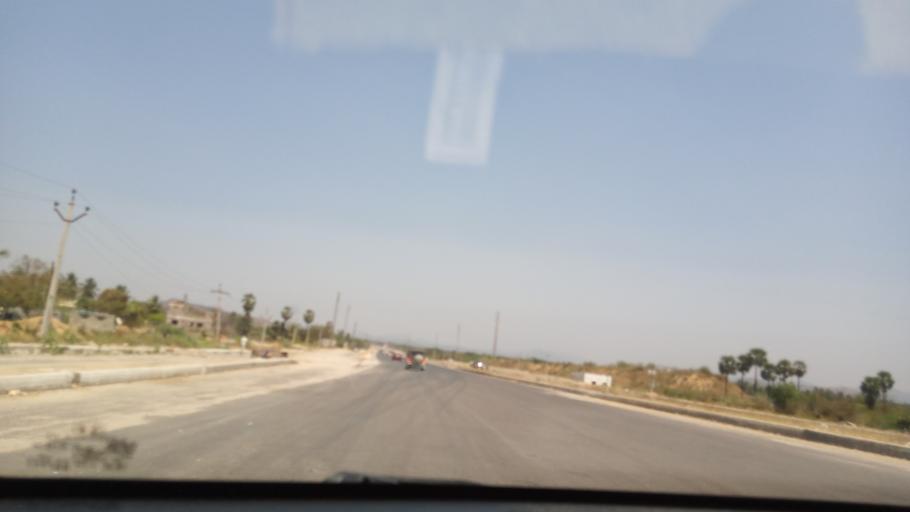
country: IN
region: Andhra Pradesh
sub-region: Chittoor
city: Pakala
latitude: 13.3581
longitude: 79.0865
